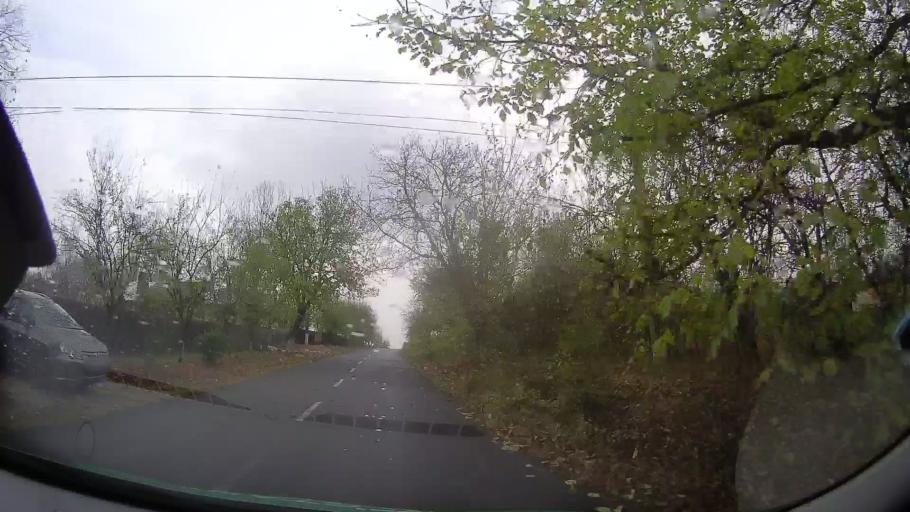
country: RO
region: Ialomita
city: Brazii
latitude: 44.7834
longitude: 26.3201
